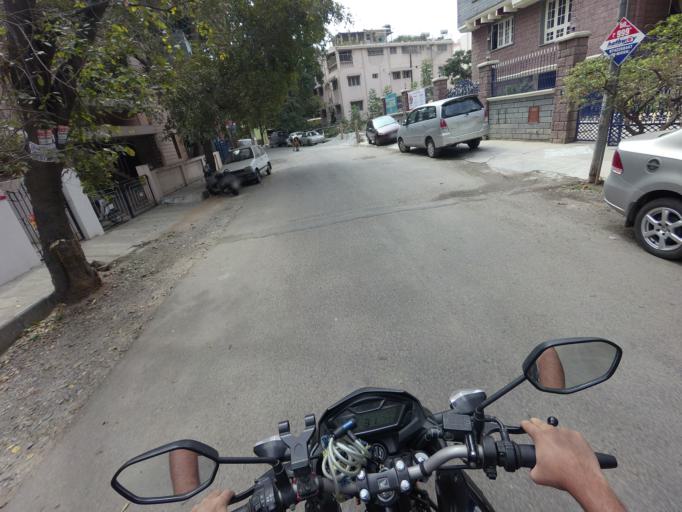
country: IN
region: Karnataka
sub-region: Bangalore Urban
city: Bangalore
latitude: 12.9604
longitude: 77.5340
